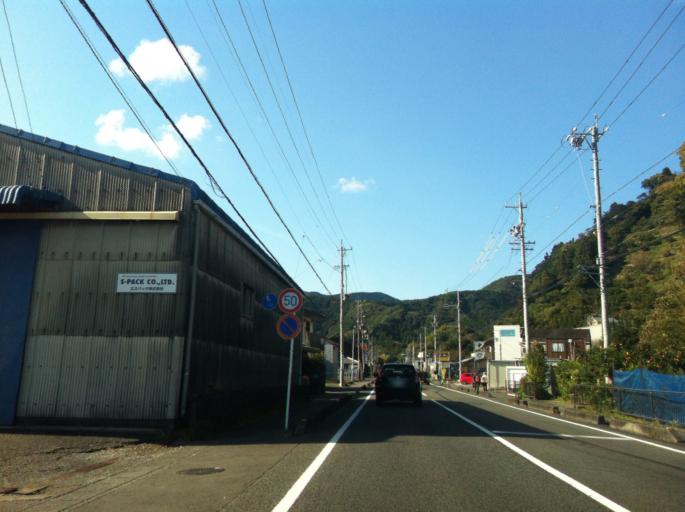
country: JP
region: Shizuoka
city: Shizuoka-shi
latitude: 34.9504
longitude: 138.3406
